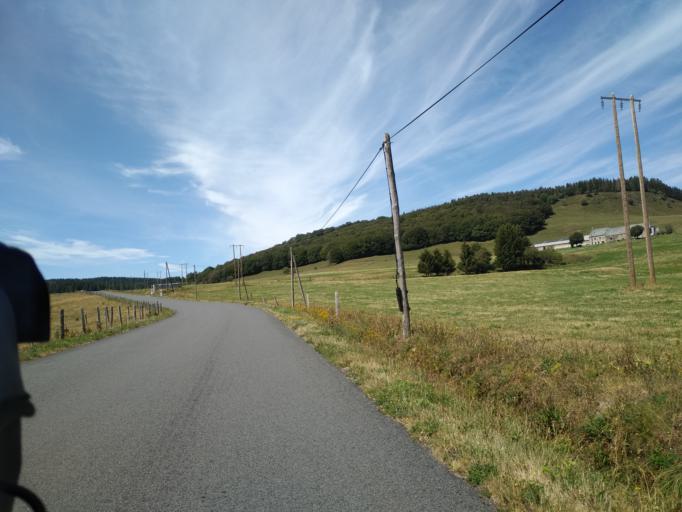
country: FR
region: Midi-Pyrenees
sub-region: Departement de l'Aveyron
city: Laguiole
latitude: 44.6777
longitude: 2.9895
